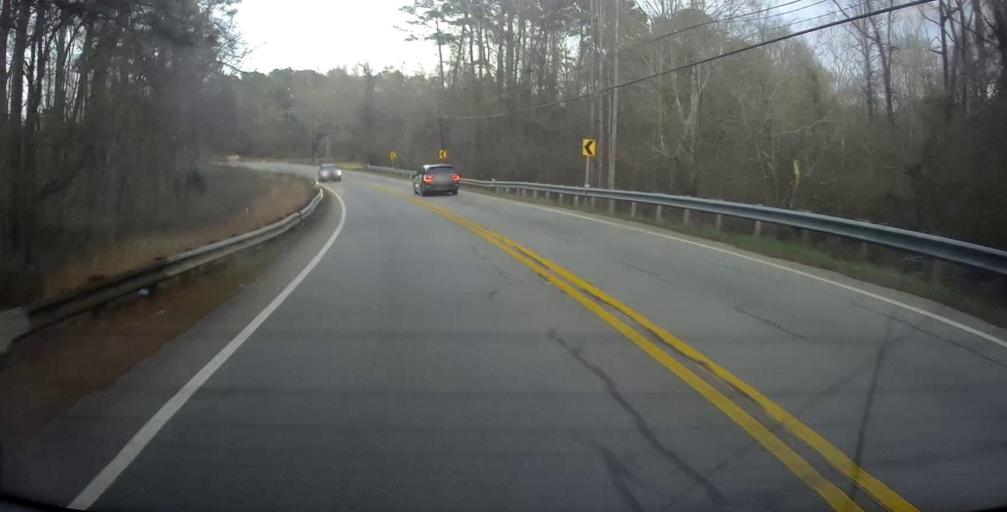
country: US
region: Alabama
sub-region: Russell County
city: Phenix City
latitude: 32.5773
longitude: -84.9127
